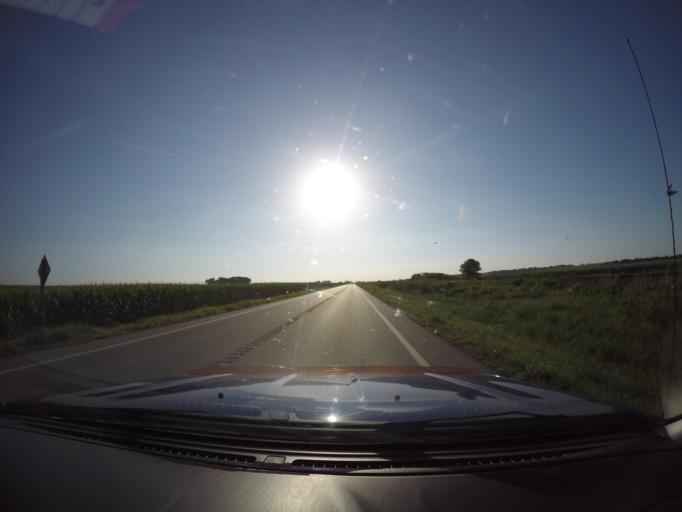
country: US
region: Kansas
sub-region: Shawnee County
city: Silver Lake
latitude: 39.1091
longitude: -95.8750
